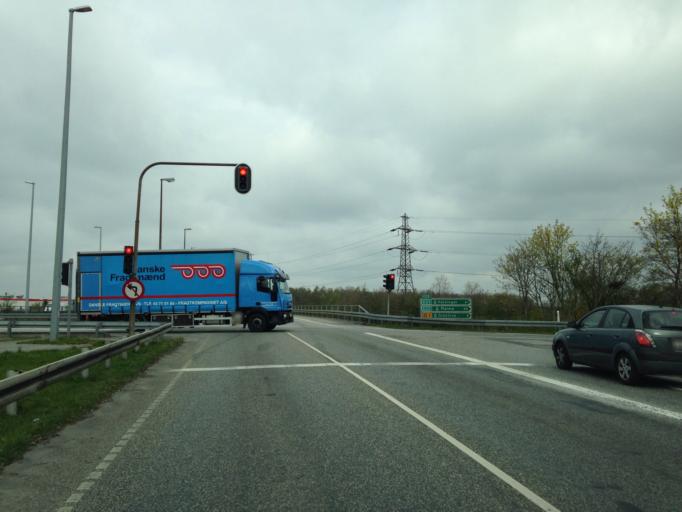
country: DK
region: Capital Region
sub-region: Ishoj Kommune
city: Ishoj
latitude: 55.6191
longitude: 12.3441
